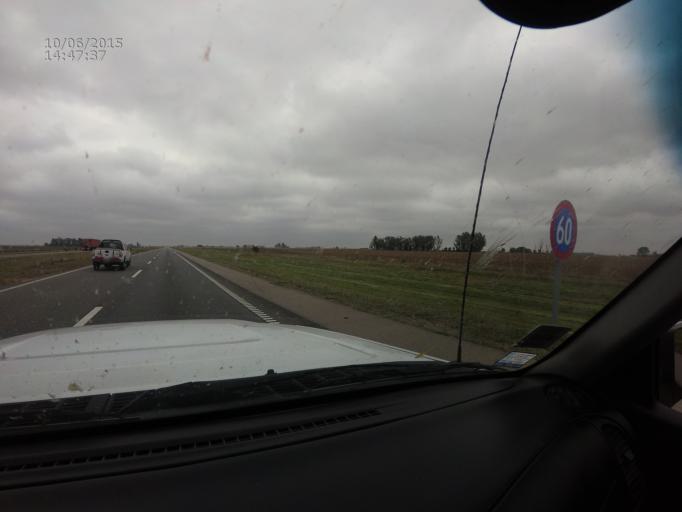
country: AR
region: Cordoba
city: Oliva
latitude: -31.9555
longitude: -63.5942
